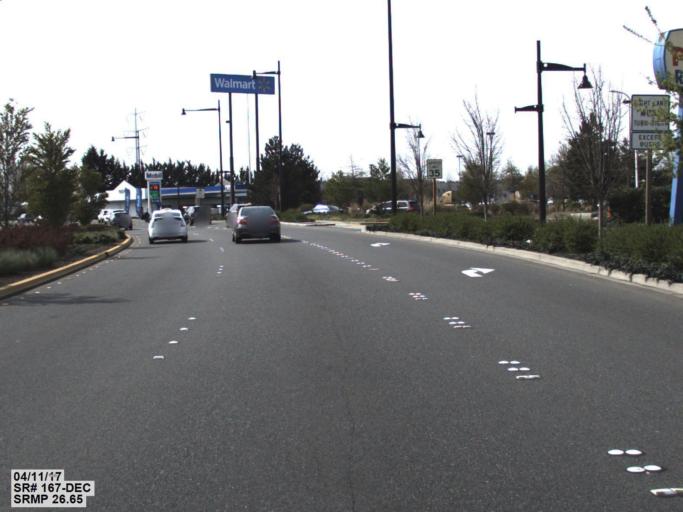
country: US
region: Washington
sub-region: King County
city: Renton
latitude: 47.4731
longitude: -122.2171
